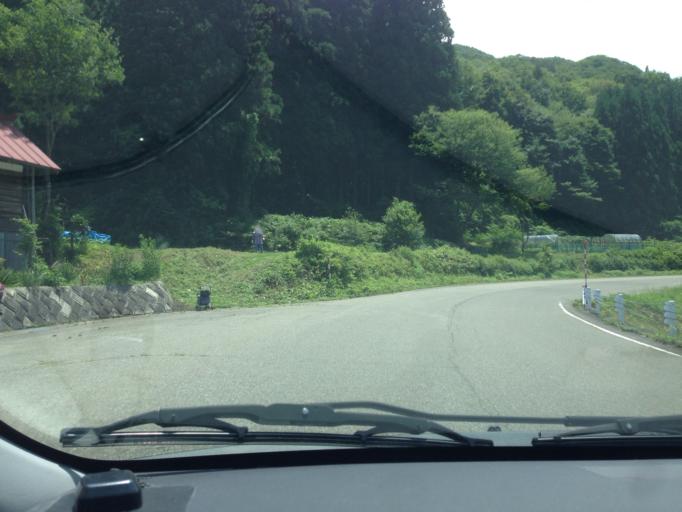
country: JP
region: Tochigi
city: Kuroiso
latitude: 37.2635
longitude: 139.8101
